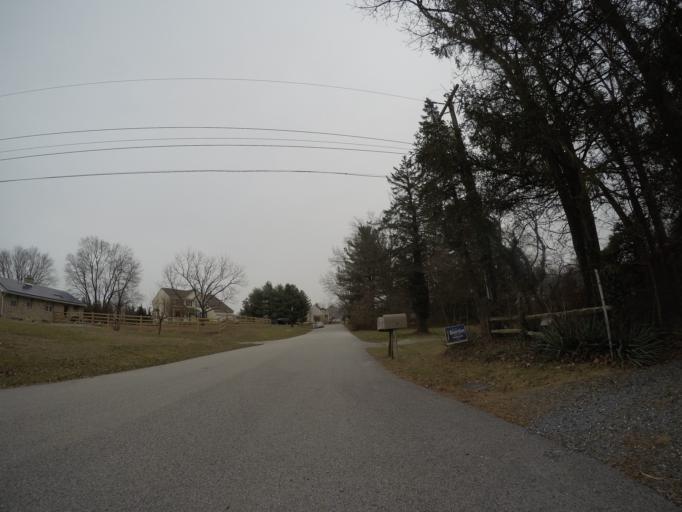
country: US
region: Maryland
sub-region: Howard County
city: Ilchester
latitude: 39.2265
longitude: -76.7854
